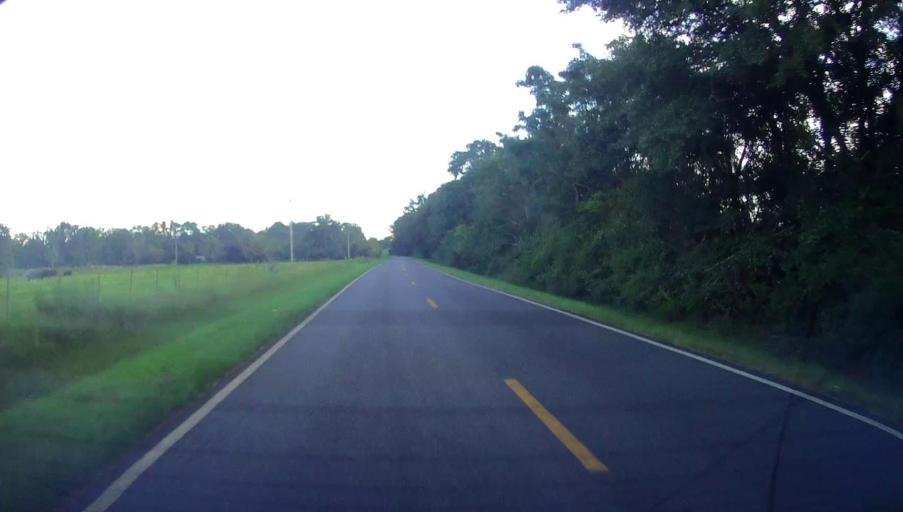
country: US
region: Georgia
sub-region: Pulaski County
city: Hawkinsville
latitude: 32.3140
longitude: -83.5525
